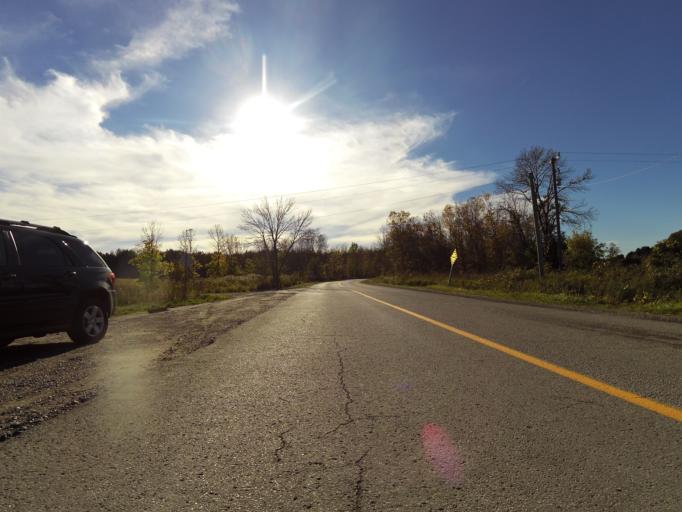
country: CA
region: Ontario
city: Oshawa
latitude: 43.8762
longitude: -78.7729
